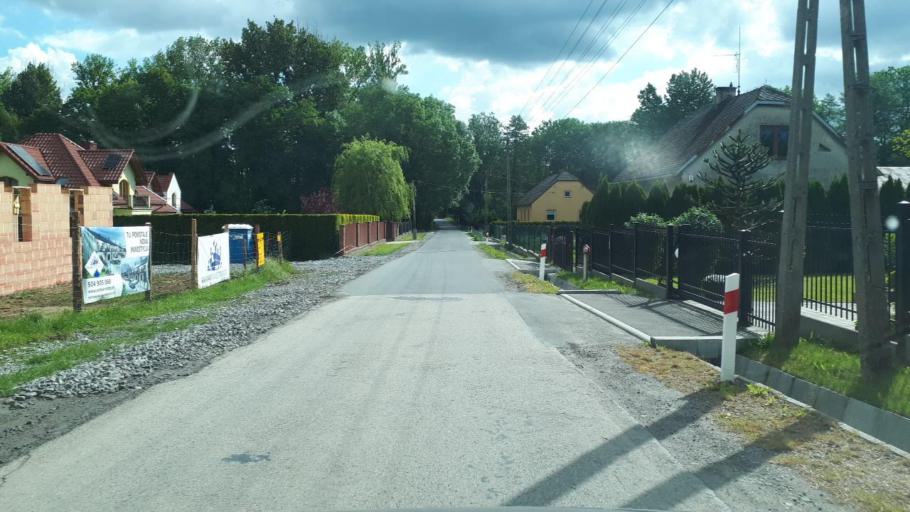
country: PL
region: Silesian Voivodeship
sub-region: Powiat bielski
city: Kozy
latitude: 49.8576
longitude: 19.1220
